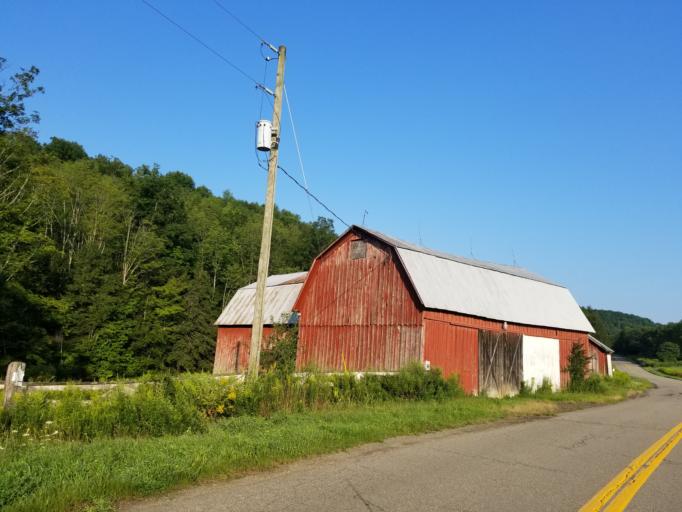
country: US
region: Pennsylvania
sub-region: Tioga County
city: Westfield
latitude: 42.0533
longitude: -77.6108
